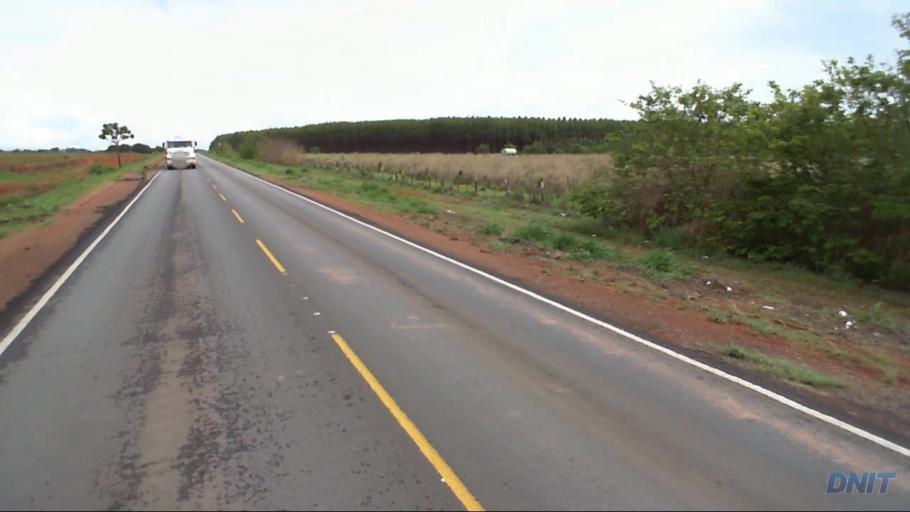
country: BR
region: Goias
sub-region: Padre Bernardo
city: Padre Bernardo
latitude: -15.2745
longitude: -48.2616
